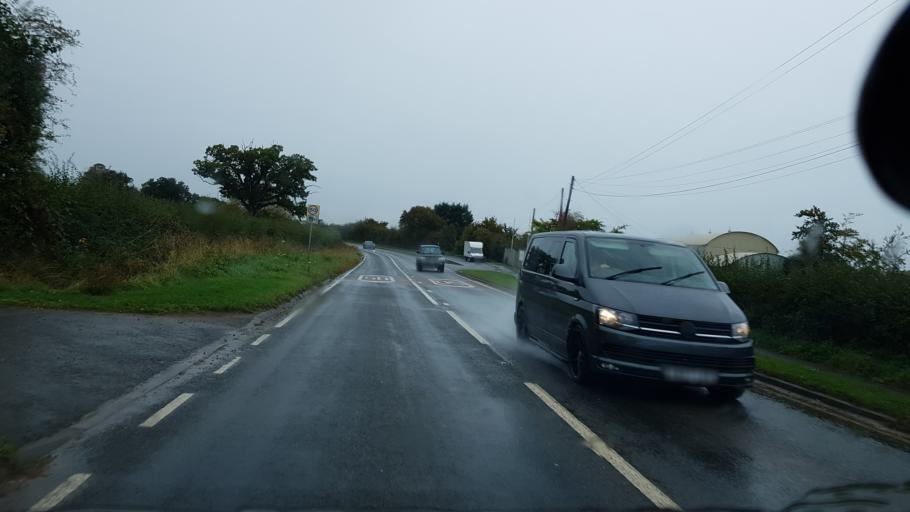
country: GB
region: England
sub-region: Worcestershire
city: Upton upon Severn
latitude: 52.0601
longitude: -2.1932
